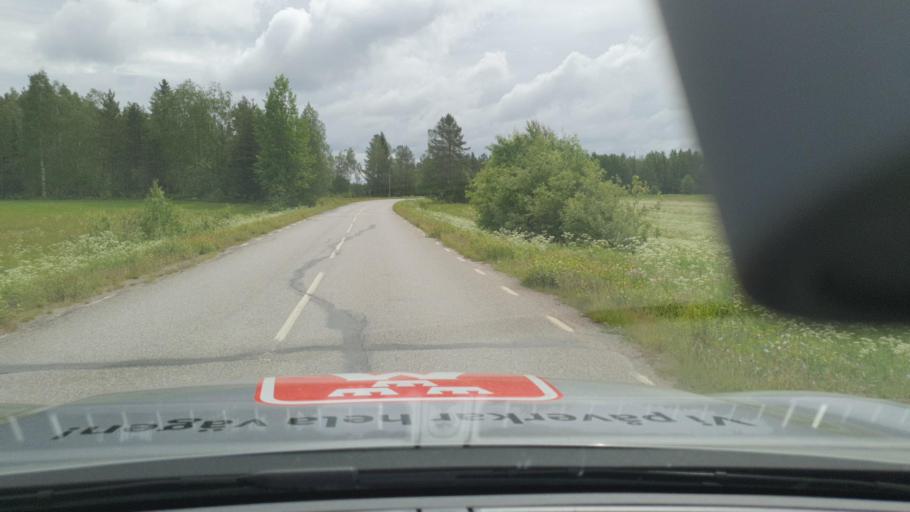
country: SE
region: Norrbotten
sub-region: Lulea Kommun
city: Ranea
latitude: 65.9357
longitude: 22.1335
